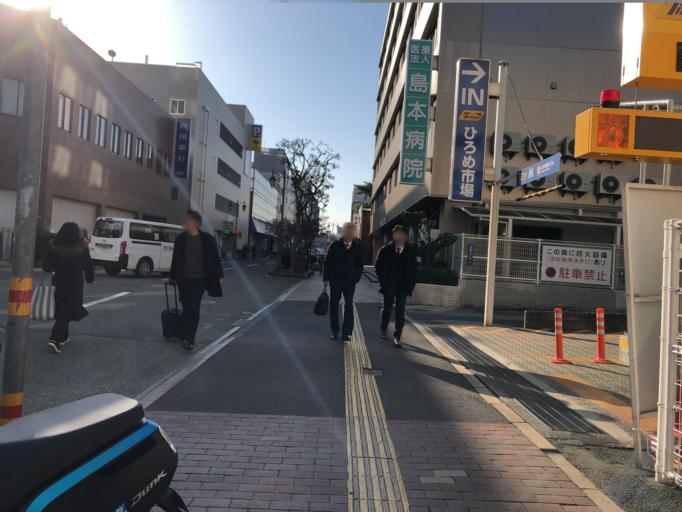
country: JP
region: Kochi
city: Kochi-shi
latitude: 33.5599
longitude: 133.5358
